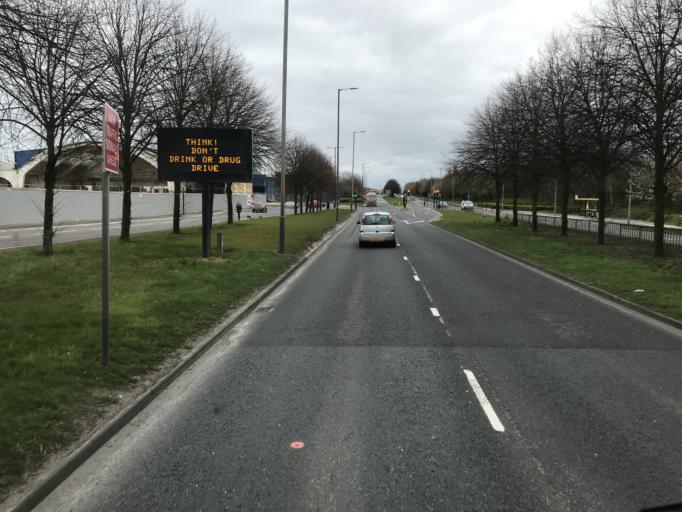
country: GB
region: England
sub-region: Borough of Halton
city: Hale
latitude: 53.3491
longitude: -2.8568
